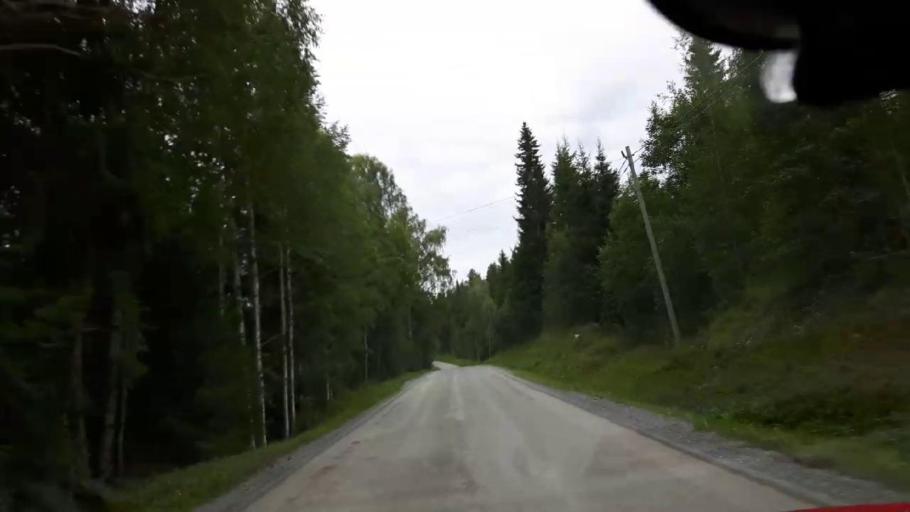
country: SE
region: Jaemtland
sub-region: Braecke Kommun
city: Braecke
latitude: 63.0878
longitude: 15.2618
